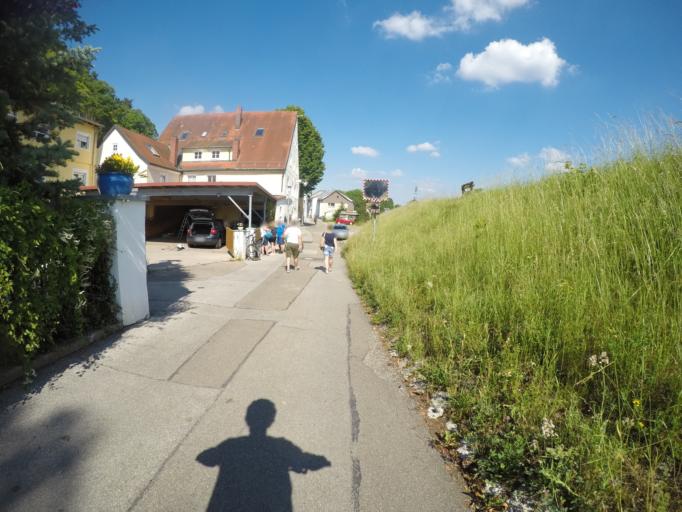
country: DE
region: Bavaria
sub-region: Lower Bavaria
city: Ihrlerstein
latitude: 48.9167
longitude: 11.8636
